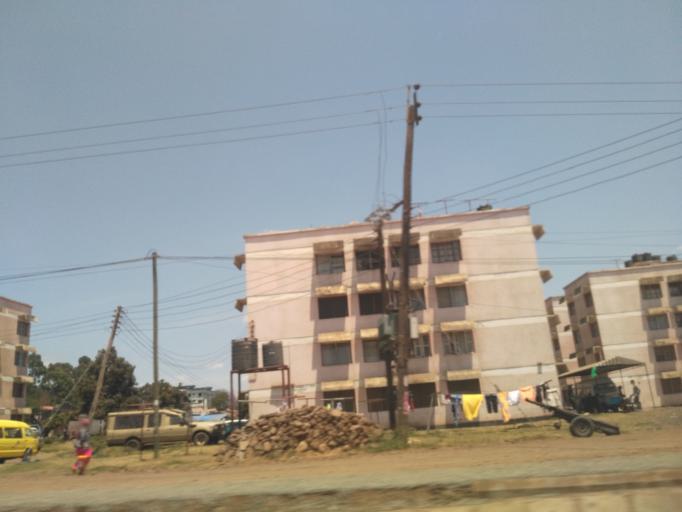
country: TZ
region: Arusha
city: Arusha
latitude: -3.3668
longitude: 36.6764
